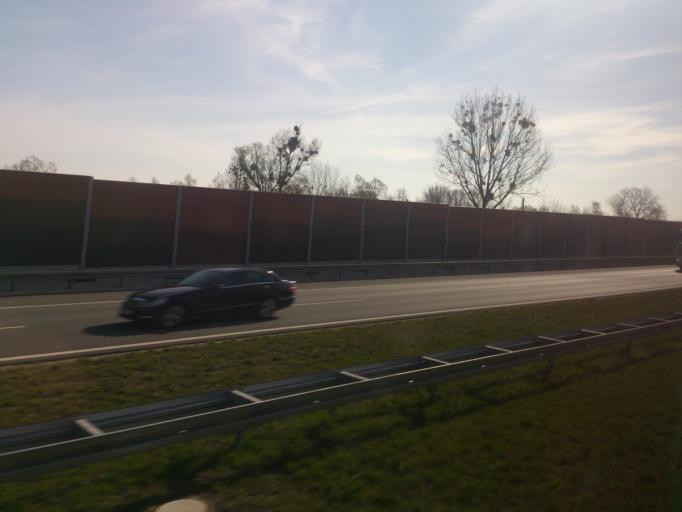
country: PL
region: Kujawsko-Pomorskie
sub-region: Powiat aleksandrowski
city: Waganiec
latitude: 52.7980
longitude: 18.8297
